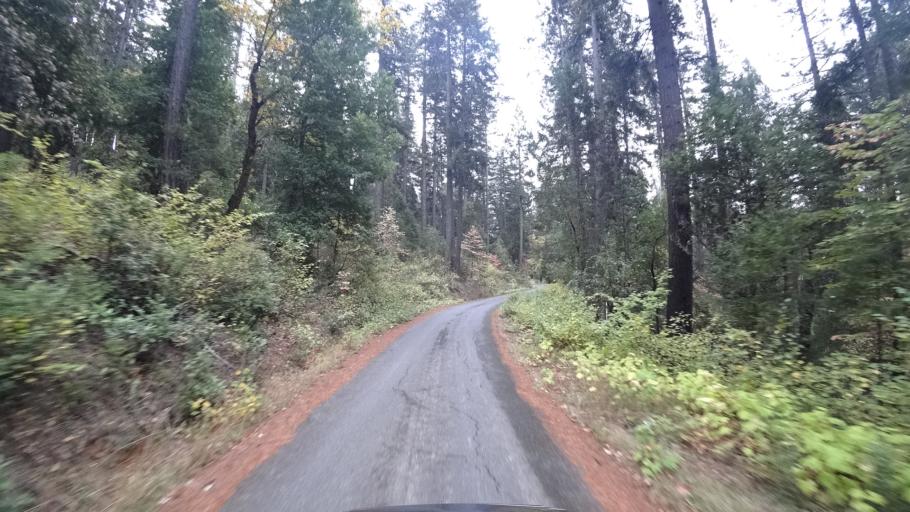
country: US
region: California
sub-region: Siskiyou County
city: Happy Camp
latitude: 41.8051
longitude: -123.3394
